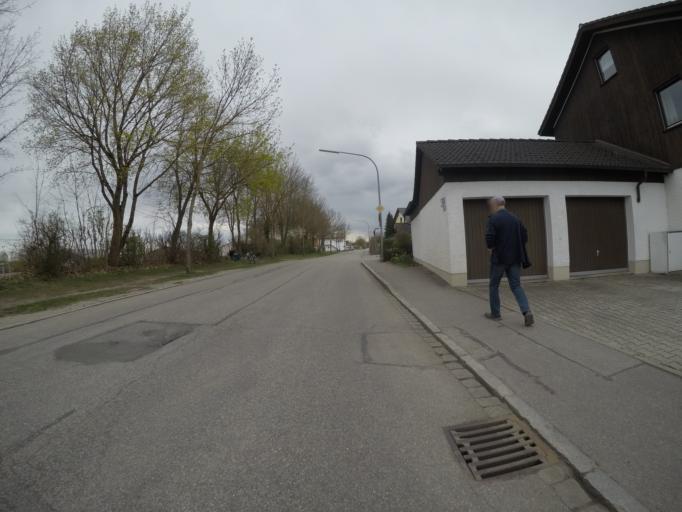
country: DE
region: Bavaria
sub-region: Lower Bavaria
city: Tiefenbach
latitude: 48.5524
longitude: 12.1076
